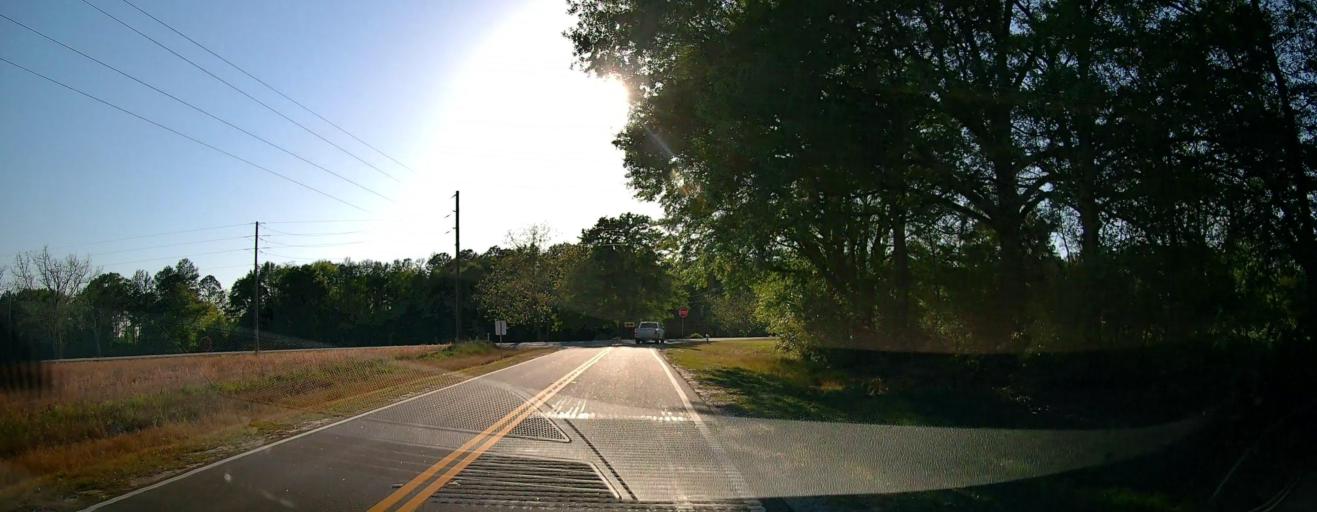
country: US
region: Georgia
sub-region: Ben Hill County
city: Fitzgerald
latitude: 31.6563
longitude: -83.1740
